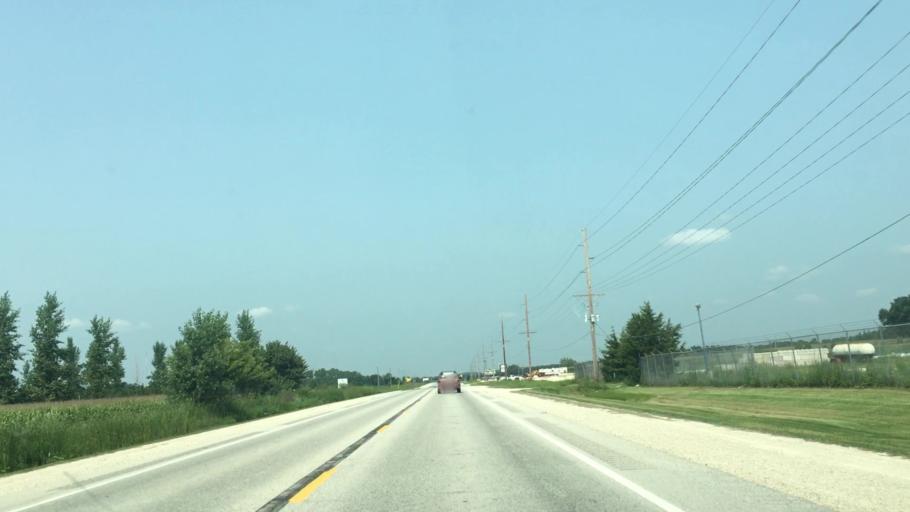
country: US
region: Iowa
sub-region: Fayette County
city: Oelwein
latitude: 42.6333
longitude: -91.9088
